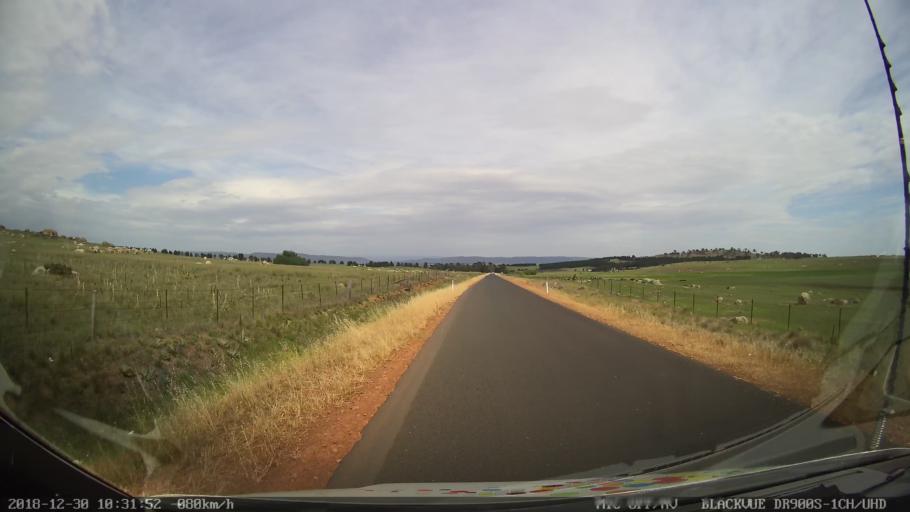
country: AU
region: New South Wales
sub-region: Snowy River
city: Berridale
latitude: -36.5042
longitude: 148.8738
